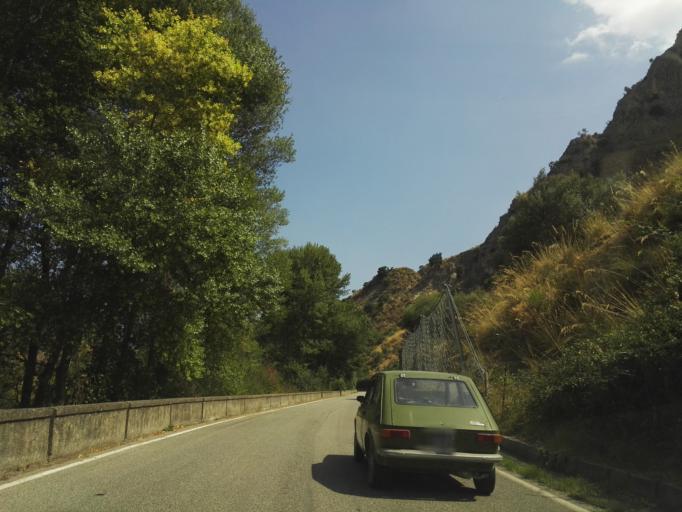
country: IT
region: Calabria
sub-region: Provincia di Reggio Calabria
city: Stilo
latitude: 38.4867
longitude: 16.4692
